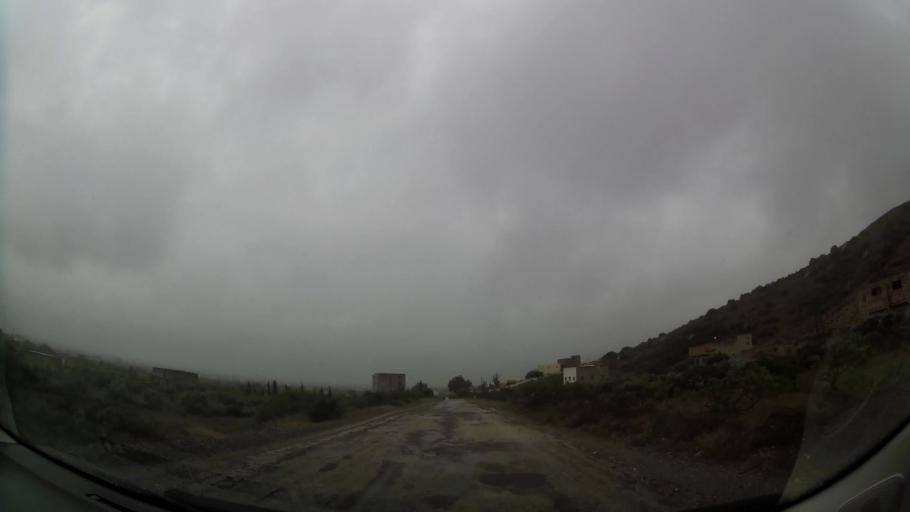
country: MA
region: Taza-Al Hoceima-Taounate
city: Imzourene
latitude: 35.1297
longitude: -3.7801
